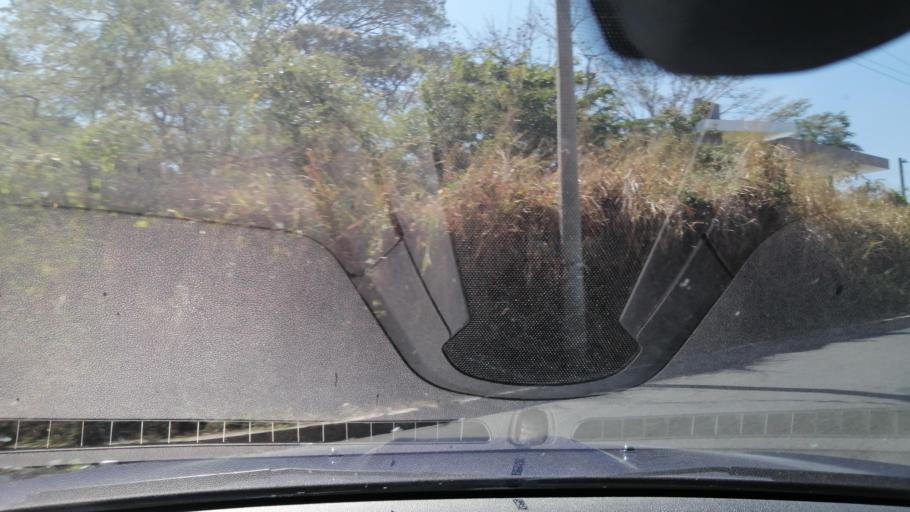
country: SV
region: Santa Ana
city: Santa Ana
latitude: 13.9623
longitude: -89.5752
